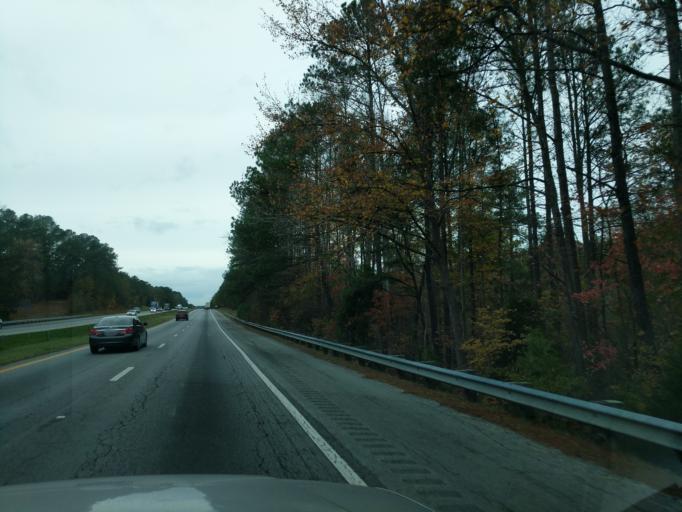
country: US
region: South Carolina
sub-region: Laurens County
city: Joanna
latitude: 34.4295
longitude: -81.7332
